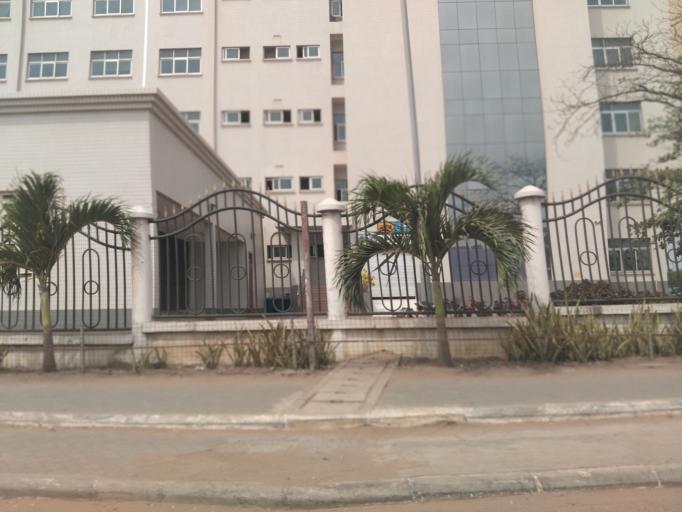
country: GH
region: Greater Accra
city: Accra
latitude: 5.5480
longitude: -0.1983
